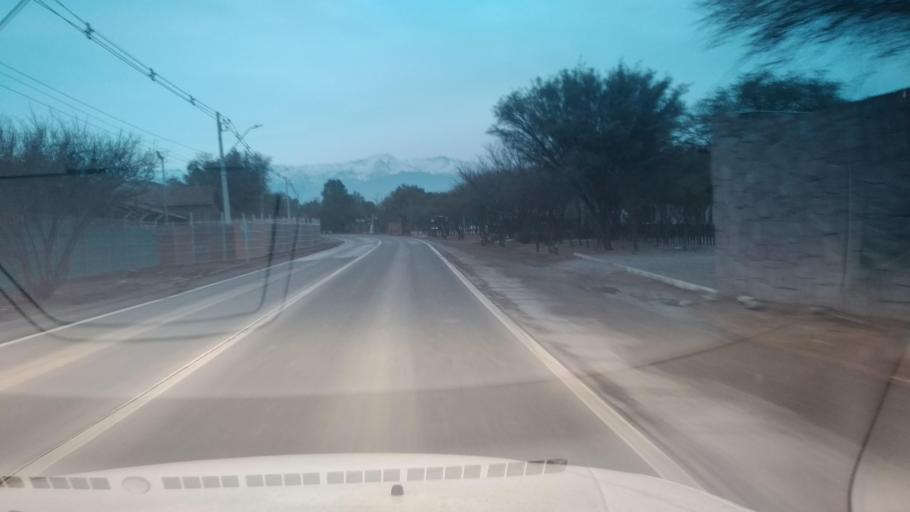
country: CL
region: Santiago Metropolitan
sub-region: Provincia de Chacabuco
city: Chicureo Abajo
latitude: -33.0920
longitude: -70.7321
